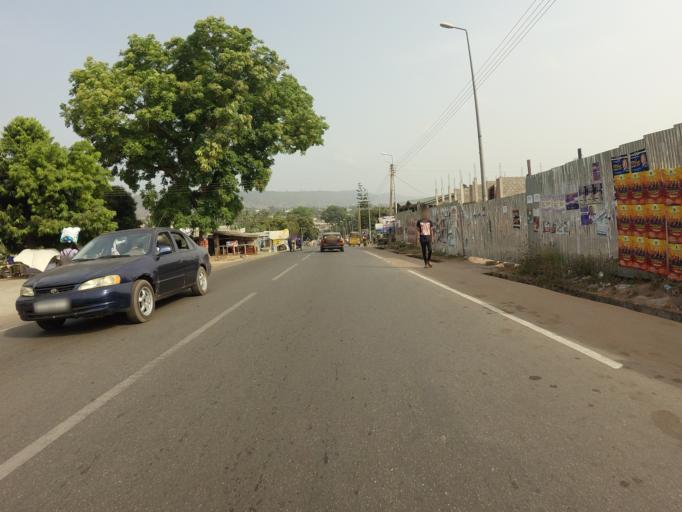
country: GH
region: Volta
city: Ho
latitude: 6.6106
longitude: 0.4749
